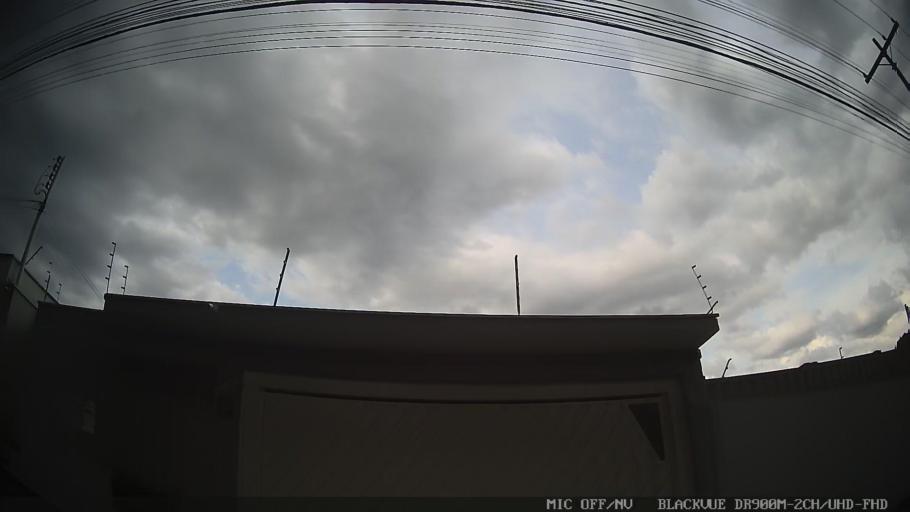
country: BR
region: Sao Paulo
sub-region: Amparo
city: Amparo
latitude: -22.7030
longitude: -46.7526
